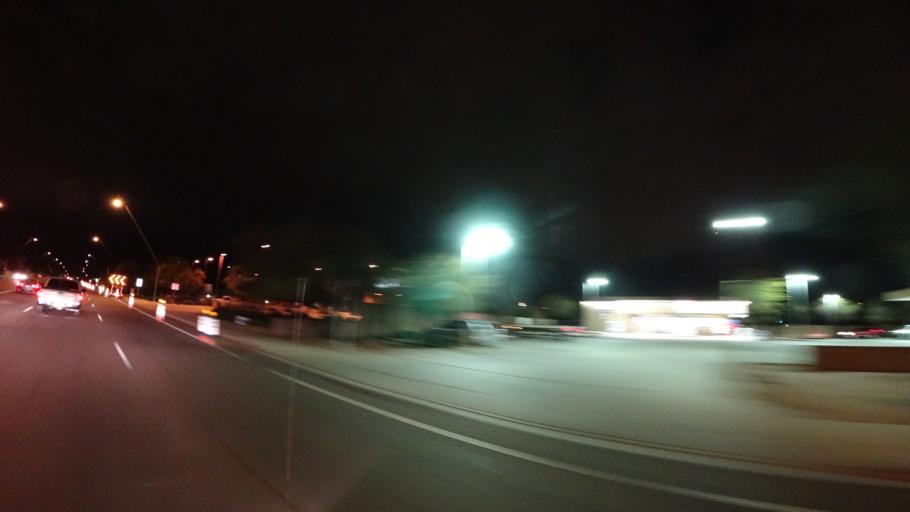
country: US
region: Arizona
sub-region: Maricopa County
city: Mesa
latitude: 33.4300
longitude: -111.8563
